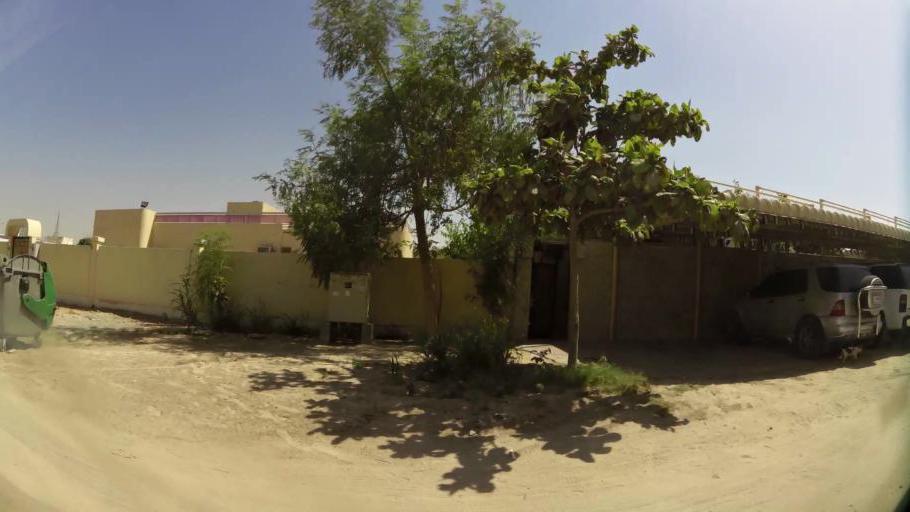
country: AE
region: Ajman
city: Ajman
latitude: 25.4084
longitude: 55.4771
